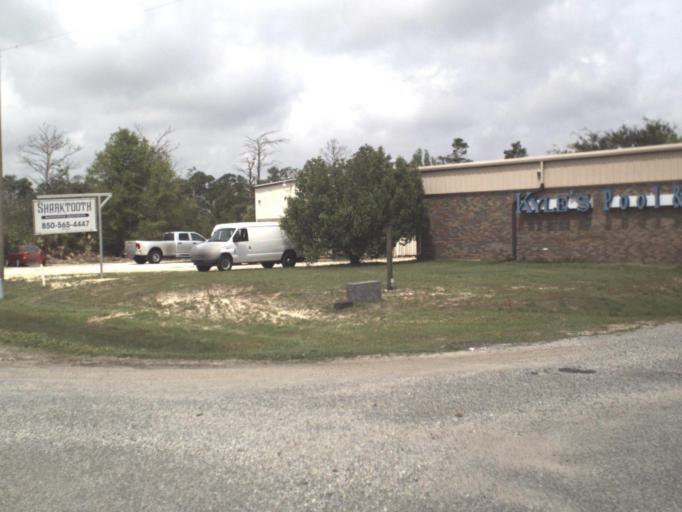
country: US
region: Florida
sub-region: Santa Rosa County
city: Tiger Point
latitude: 30.3926
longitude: -87.0488
